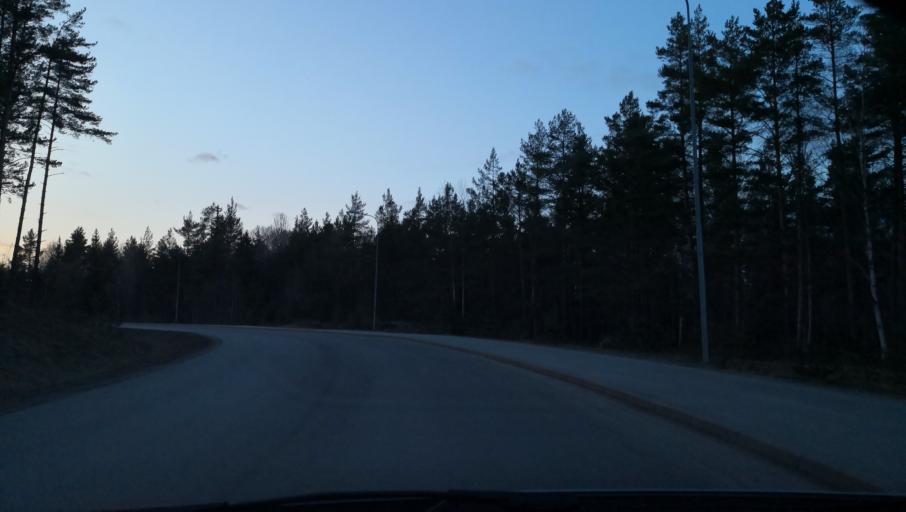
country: SE
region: Stockholm
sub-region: Nacka Kommun
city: Boo
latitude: 59.3404
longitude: 18.2980
